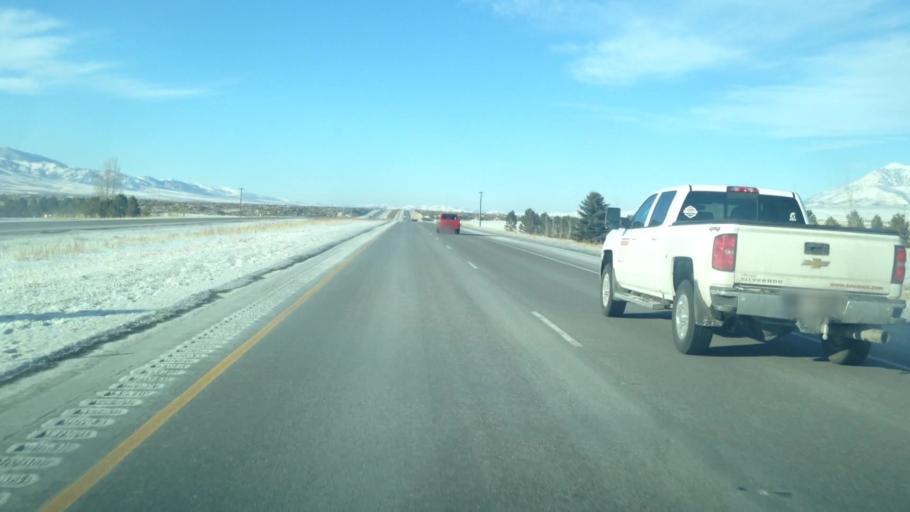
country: US
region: Idaho
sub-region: Bannock County
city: Pocatello
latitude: 42.5808
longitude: -112.1853
